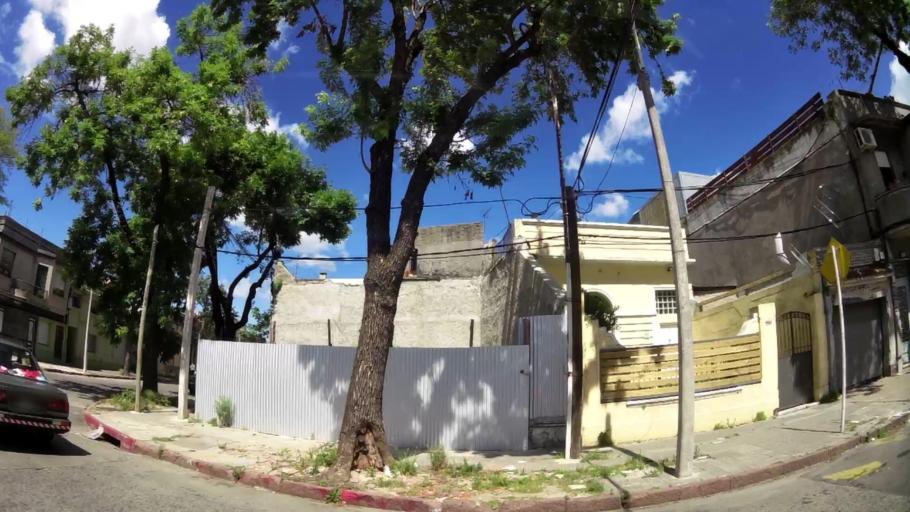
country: UY
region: Montevideo
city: Montevideo
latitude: -34.8820
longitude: -56.1920
